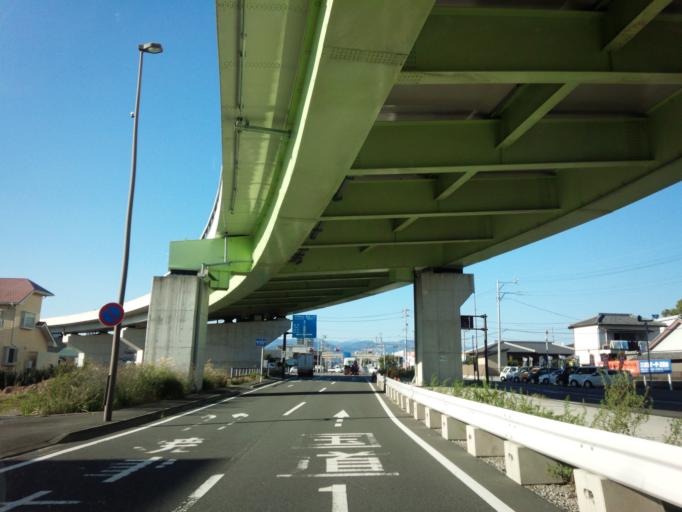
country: JP
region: Shizuoka
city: Shizuoka-shi
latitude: 34.9391
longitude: 138.3970
